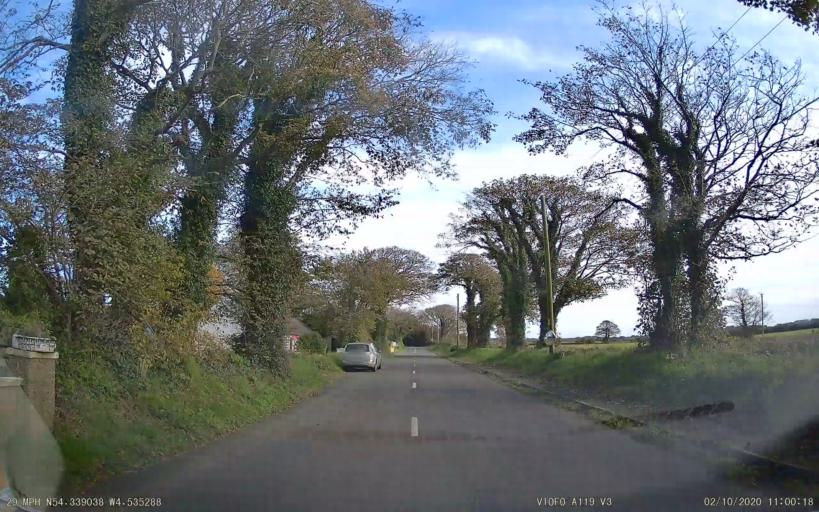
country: IM
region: Ramsey
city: Ramsey
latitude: 54.3390
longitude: -4.5353
